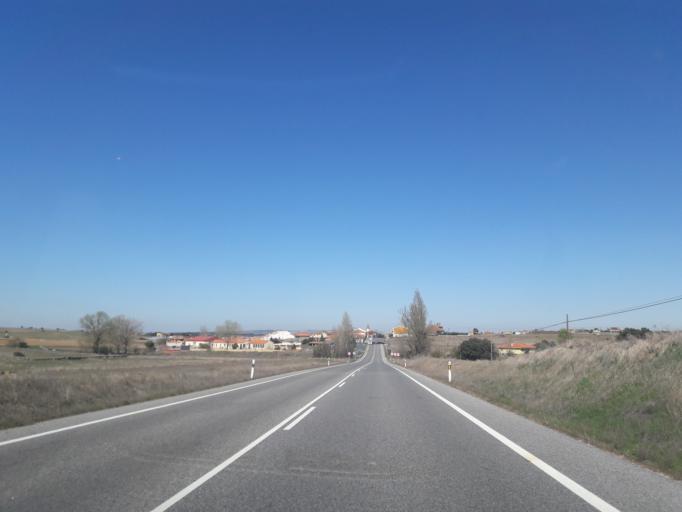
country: ES
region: Castille and Leon
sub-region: Provincia de Salamanca
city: Mozarbez
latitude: 40.8522
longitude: -5.6475
